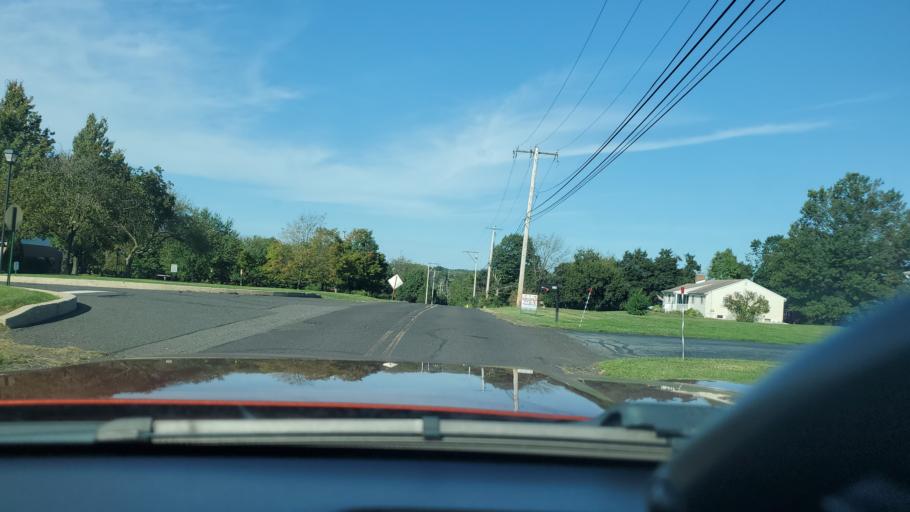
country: US
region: Pennsylvania
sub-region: Montgomery County
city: Limerick
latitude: 40.3007
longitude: -75.5255
